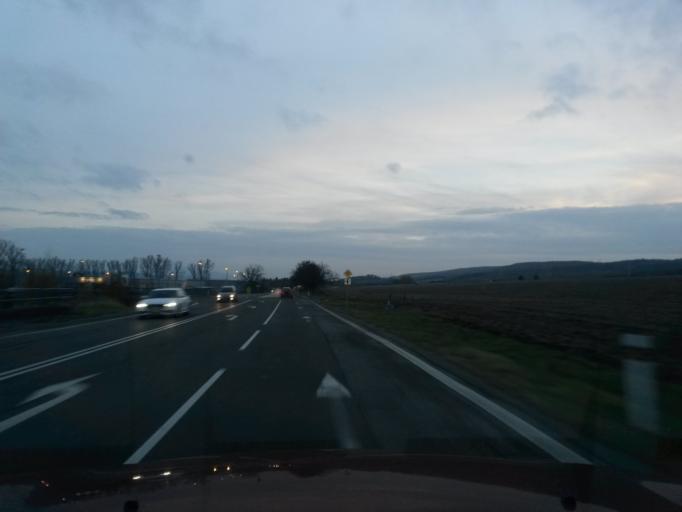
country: SK
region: Kosicky
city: Kosice
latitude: 48.7940
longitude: 21.3060
